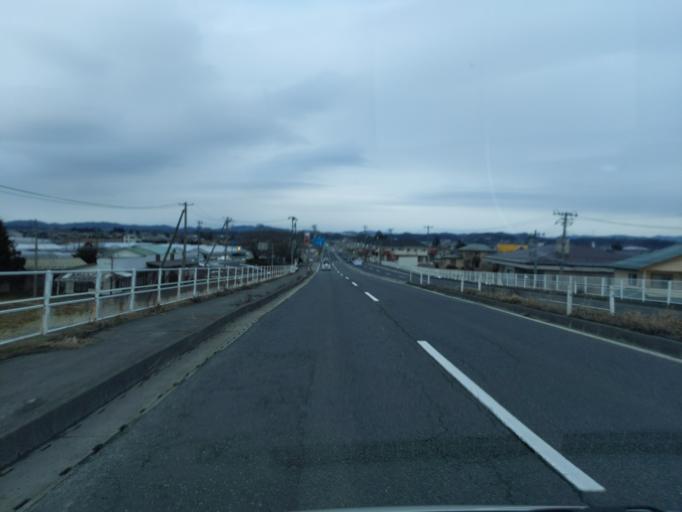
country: JP
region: Iwate
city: Mizusawa
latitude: 39.1718
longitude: 141.1573
